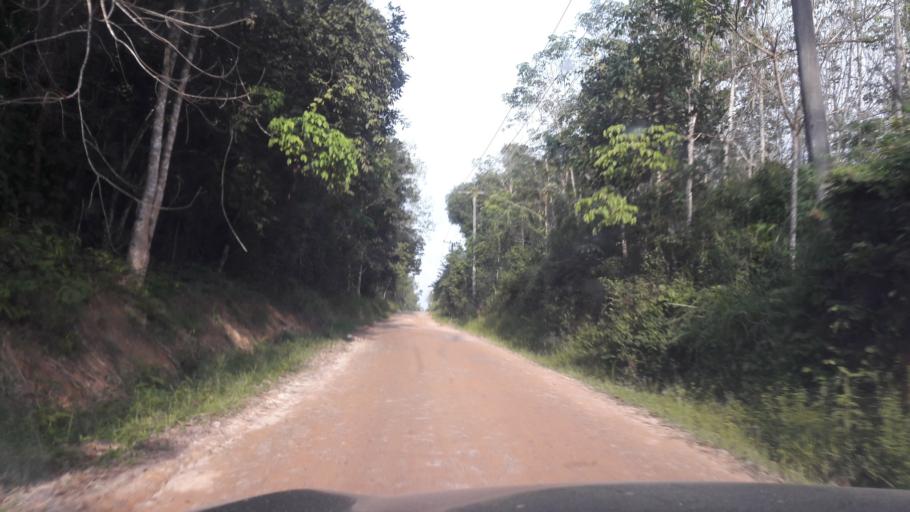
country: ID
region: South Sumatra
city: Gunungmenang
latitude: -3.2552
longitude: 104.0227
